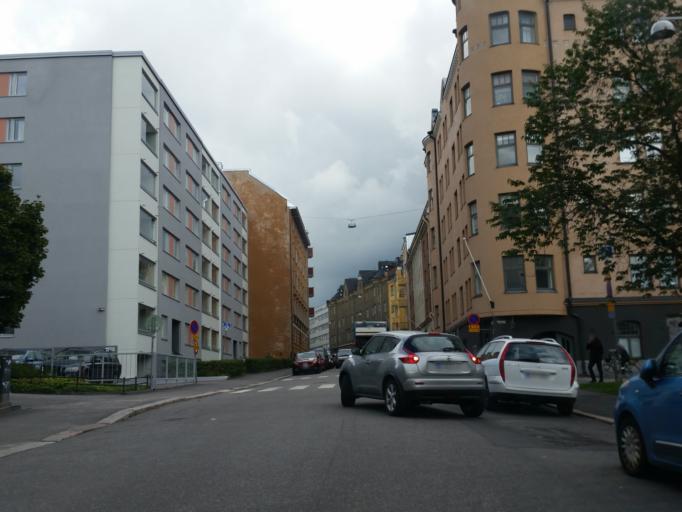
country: FI
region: Uusimaa
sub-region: Helsinki
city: Helsinki
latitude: 60.1600
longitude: 24.9332
